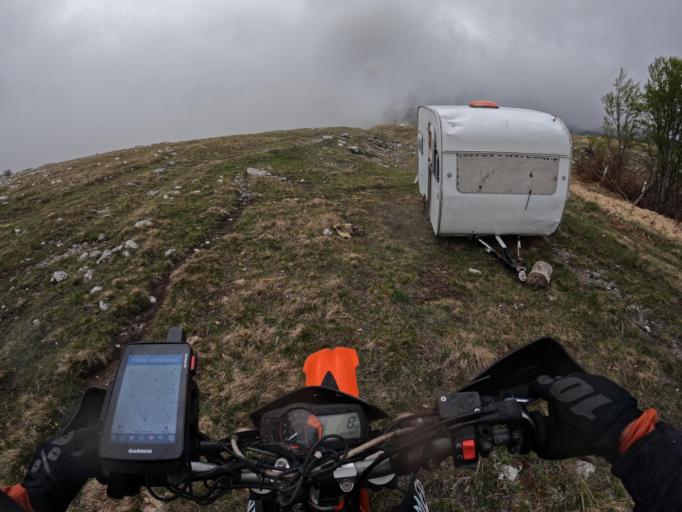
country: HR
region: Zadarska
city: Gracac
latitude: 44.3981
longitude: 15.9808
